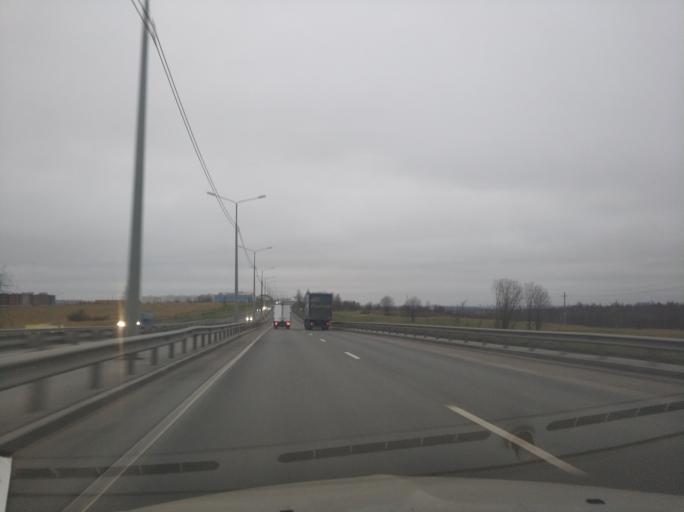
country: RU
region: St.-Petersburg
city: Pushkin
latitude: 59.7563
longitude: 30.3819
